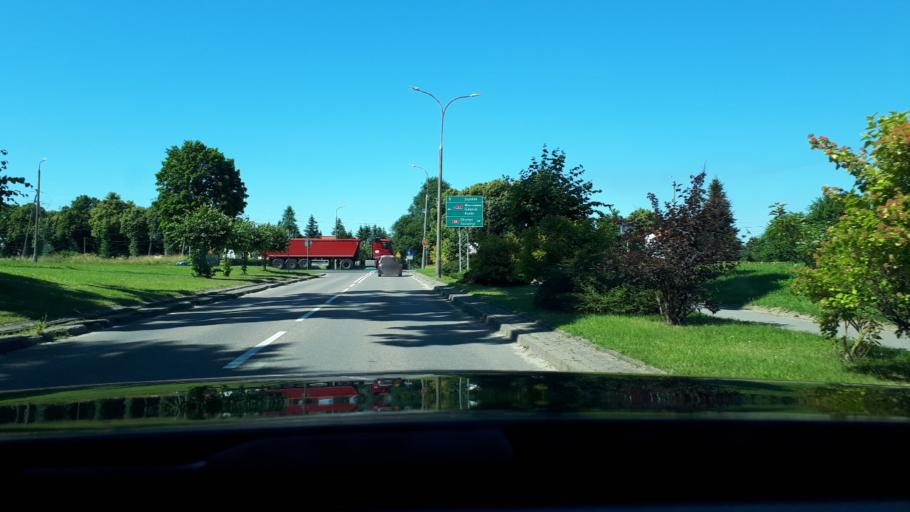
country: PL
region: Warmian-Masurian Voivodeship
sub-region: Powiat olsztynski
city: Olsztynek
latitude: 53.5849
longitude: 20.2845
